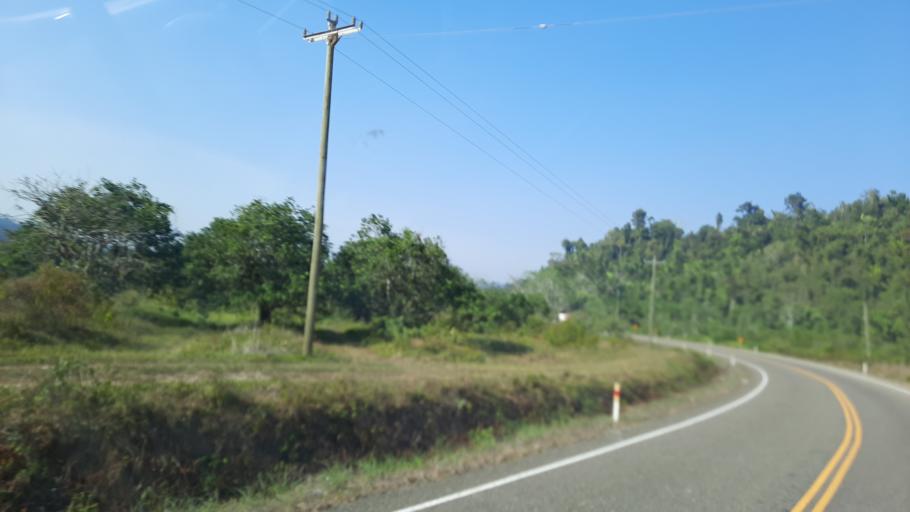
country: BZ
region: Cayo
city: Belmopan
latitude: 17.1468
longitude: -88.6967
